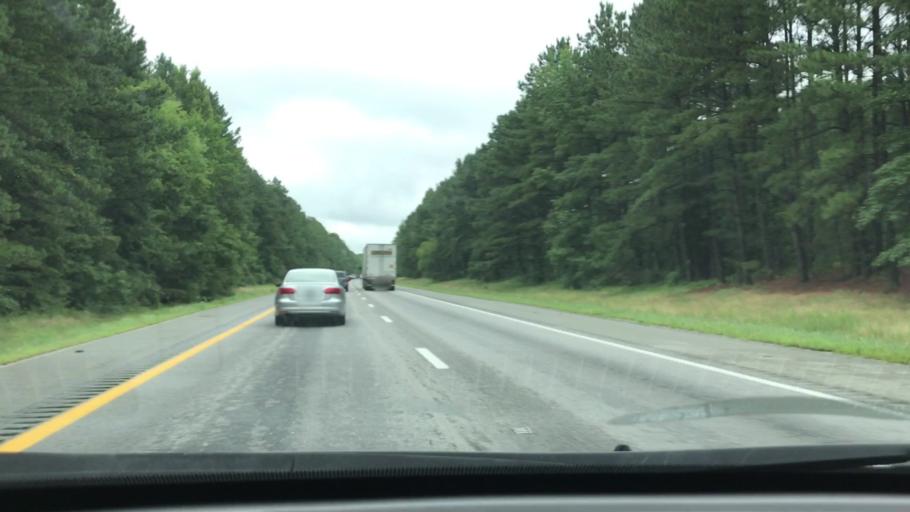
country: US
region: Virginia
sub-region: City of Emporia
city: Emporia
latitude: 36.7905
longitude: -77.4614
